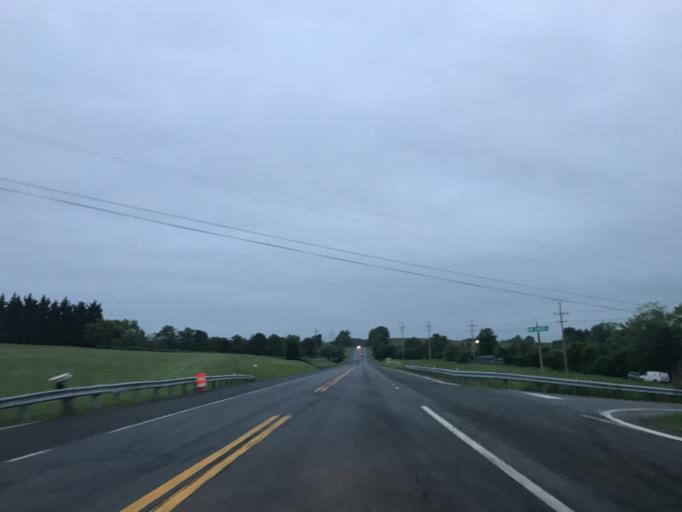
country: US
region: Maryland
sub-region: Frederick County
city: Linganore
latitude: 39.4045
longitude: -77.2581
